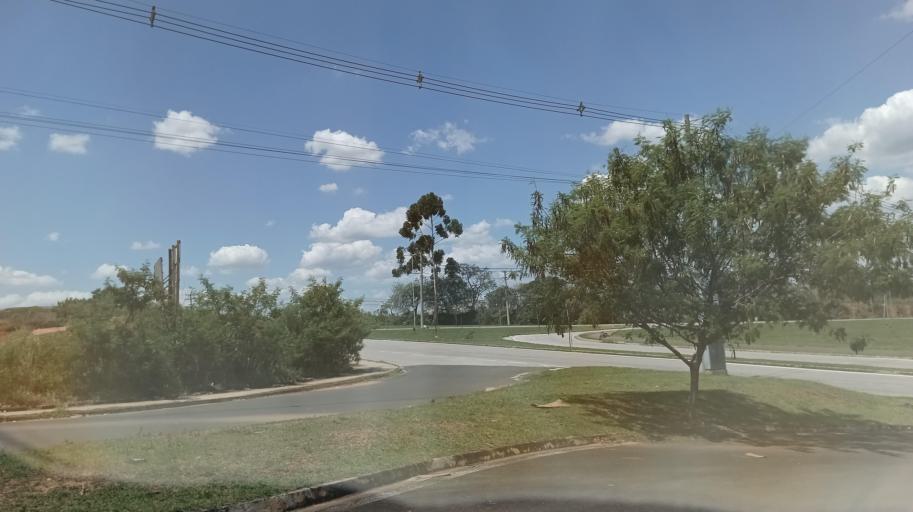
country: BR
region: Sao Paulo
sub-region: Sorocaba
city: Sorocaba
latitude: -23.4675
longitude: -47.4539
